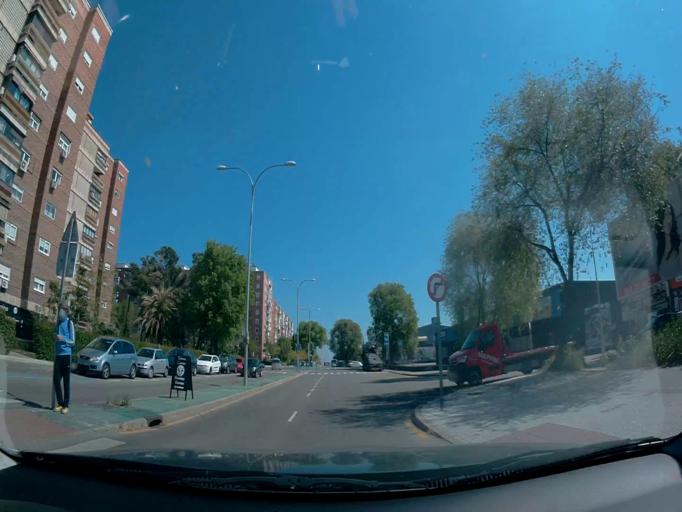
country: ES
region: Madrid
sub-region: Provincia de Madrid
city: Alcorcon
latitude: 40.3487
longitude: -3.8035
